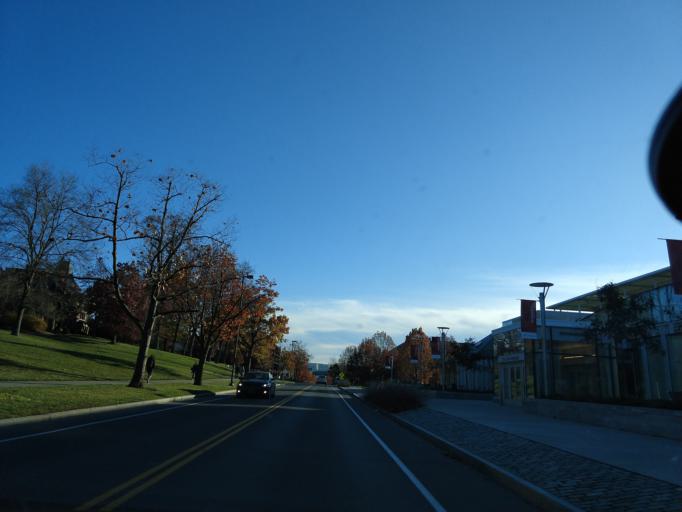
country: US
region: New York
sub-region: Tompkins County
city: East Ithaca
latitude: 42.4494
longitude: -76.4829
